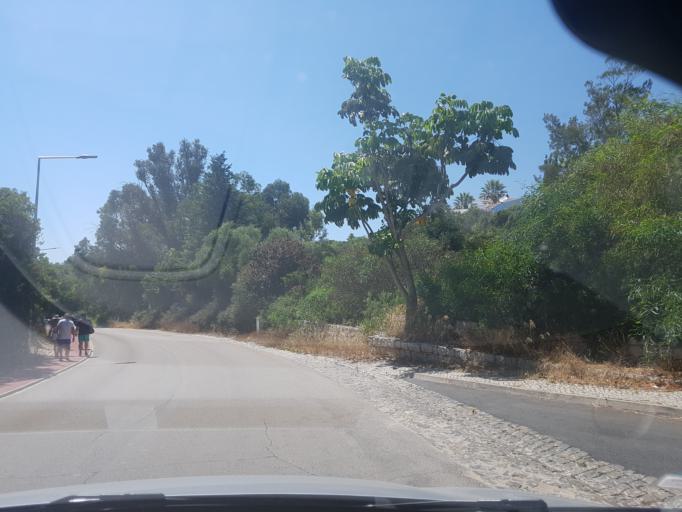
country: PT
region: Faro
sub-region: Lagoa
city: Carvoeiro
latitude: 37.0936
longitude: -8.4491
